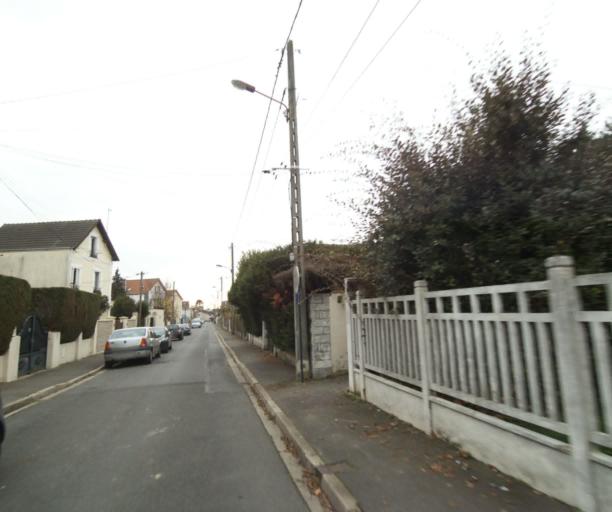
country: FR
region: Ile-de-France
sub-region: Departement du Val-d'Oise
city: Arnouville
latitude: 48.9996
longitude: 2.4184
